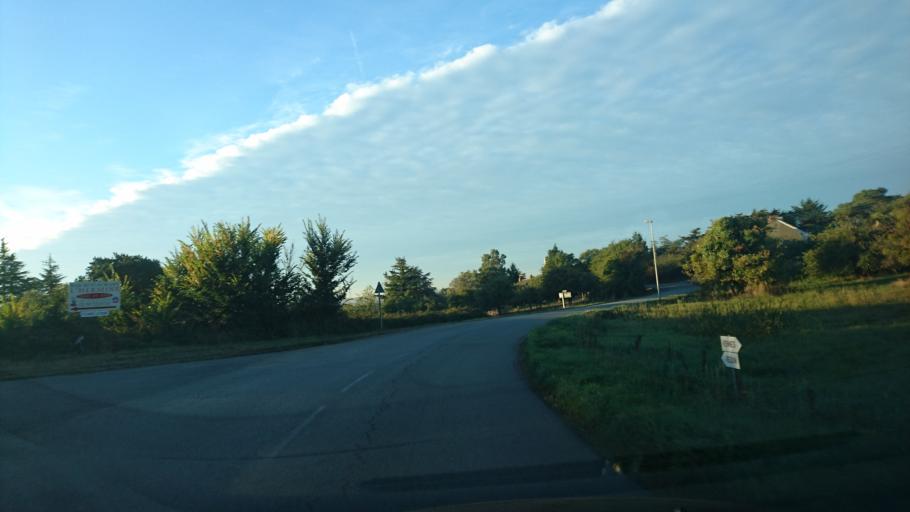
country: FR
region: Brittany
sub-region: Departement d'Ille-et-Vilaine
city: Sainte-Marie
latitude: 47.7181
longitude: -1.9777
